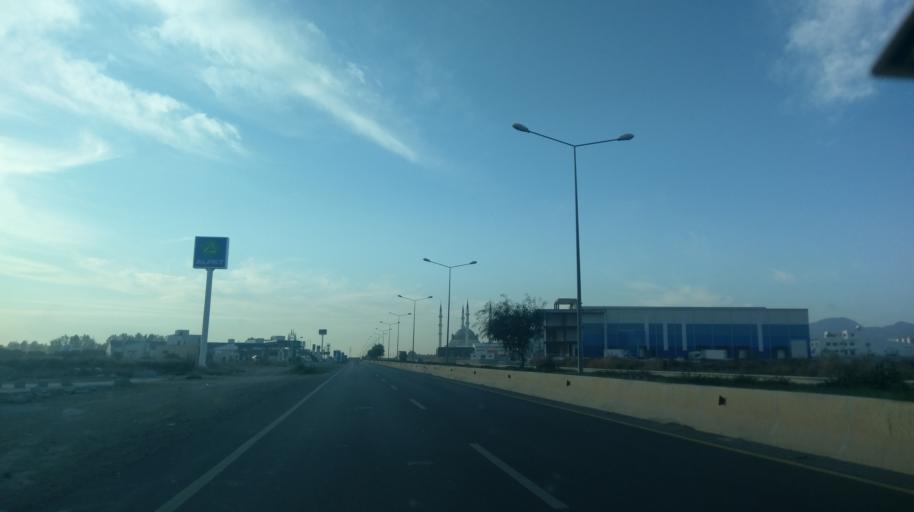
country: CY
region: Lefkosia
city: Nicosia
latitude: 35.2152
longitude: 33.4318
